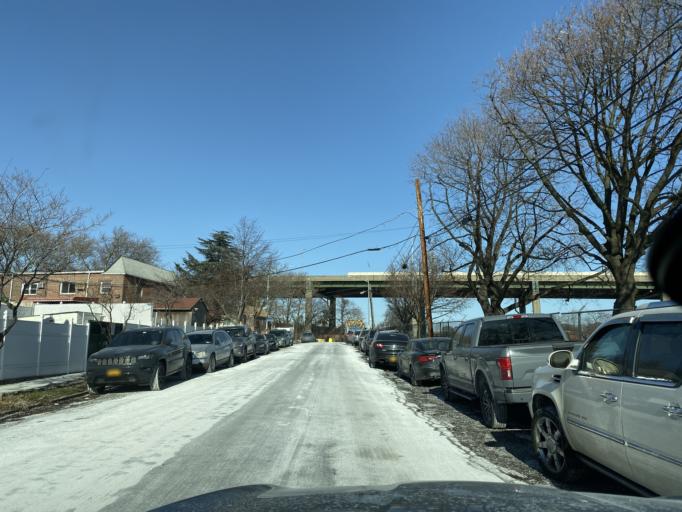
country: US
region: New York
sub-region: Queens County
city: Long Island City
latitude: 40.7300
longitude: -73.9177
